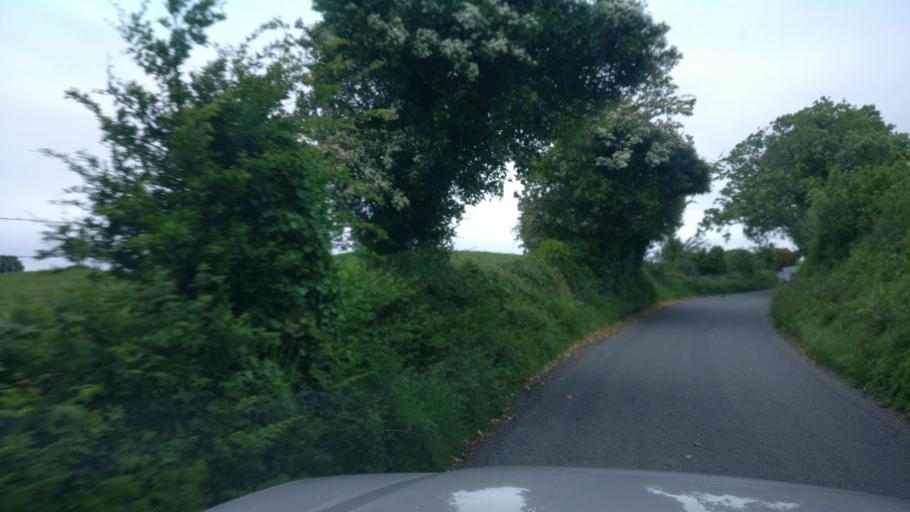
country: IE
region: Connaught
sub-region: County Galway
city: Loughrea
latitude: 53.1222
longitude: -8.4404
